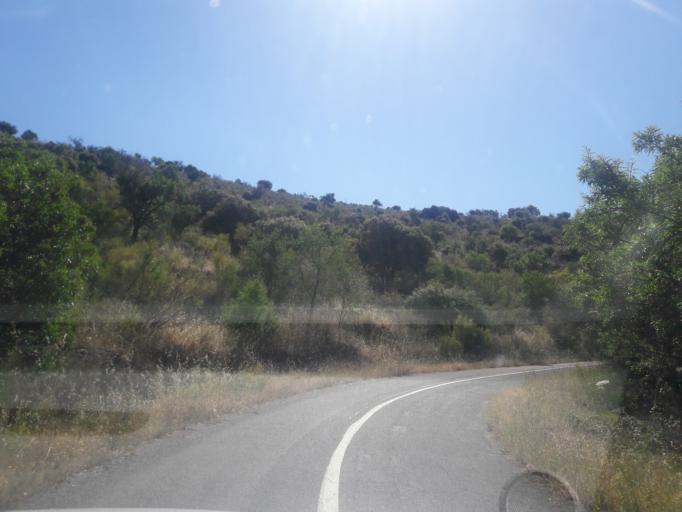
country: ES
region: Castille and Leon
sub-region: Provincia de Salamanca
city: Saucelle
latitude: 41.0175
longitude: -6.7491
